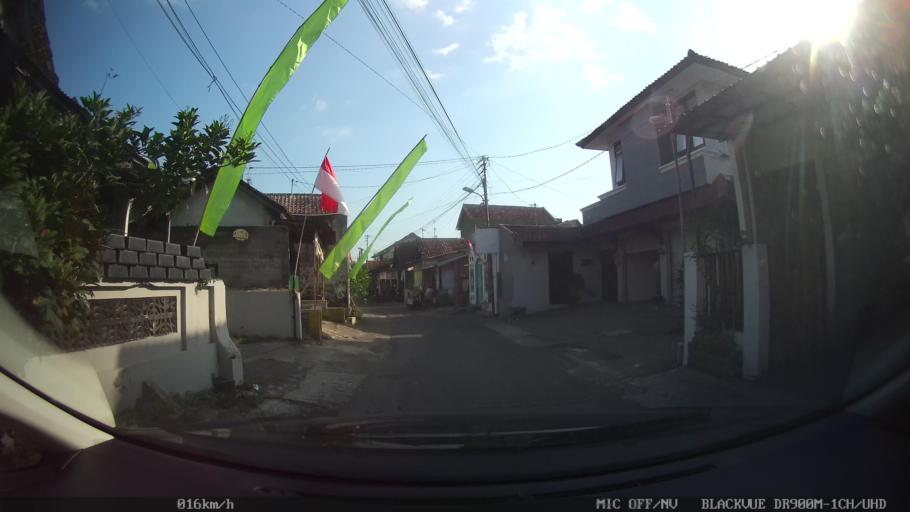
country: ID
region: Daerah Istimewa Yogyakarta
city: Yogyakarta
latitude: -7.7994
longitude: 110.3484
